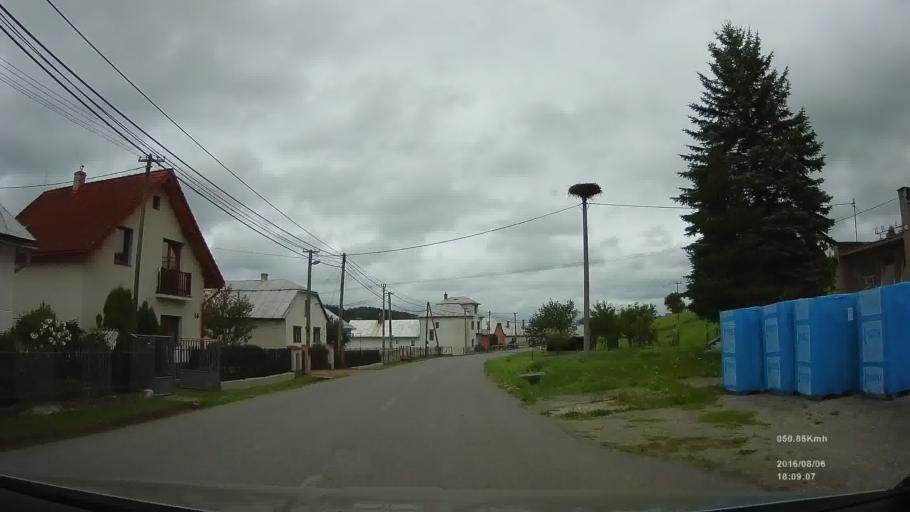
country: SK
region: Presovsky
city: Svidnik
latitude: 49.3821
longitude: 21.5706
